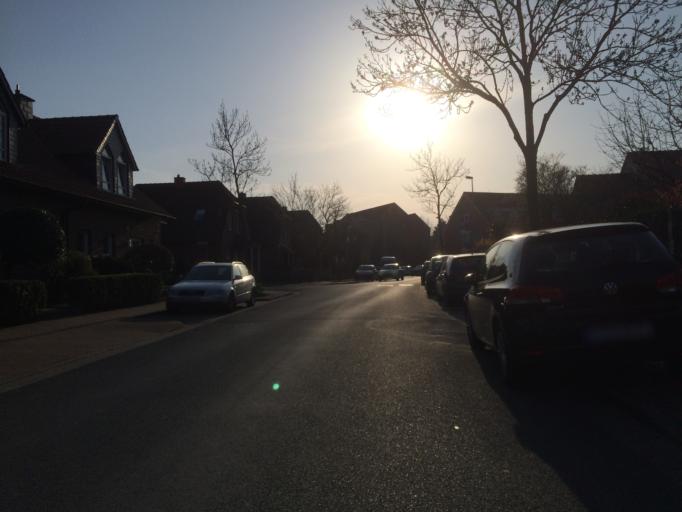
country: DE
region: Lower Saxony
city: Gehrden
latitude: 52.3087
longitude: 9.6105
